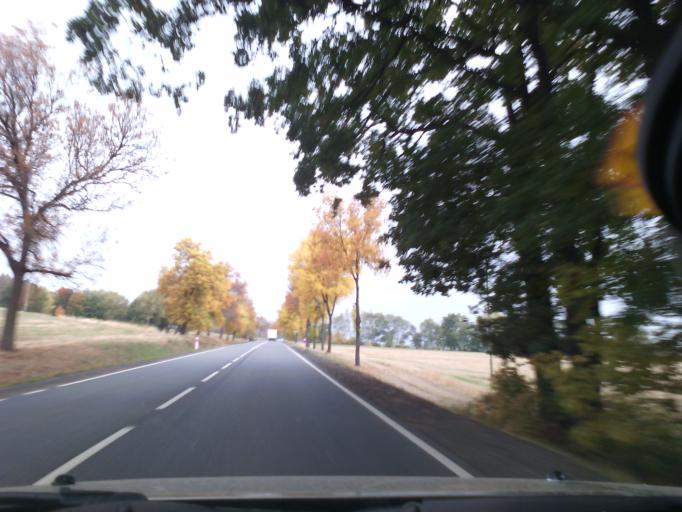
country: PL
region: Lower Silesian Voivodeship
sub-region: Powiat swidnicki
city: Swiebodzice
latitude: 50.8795
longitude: 16.2779
